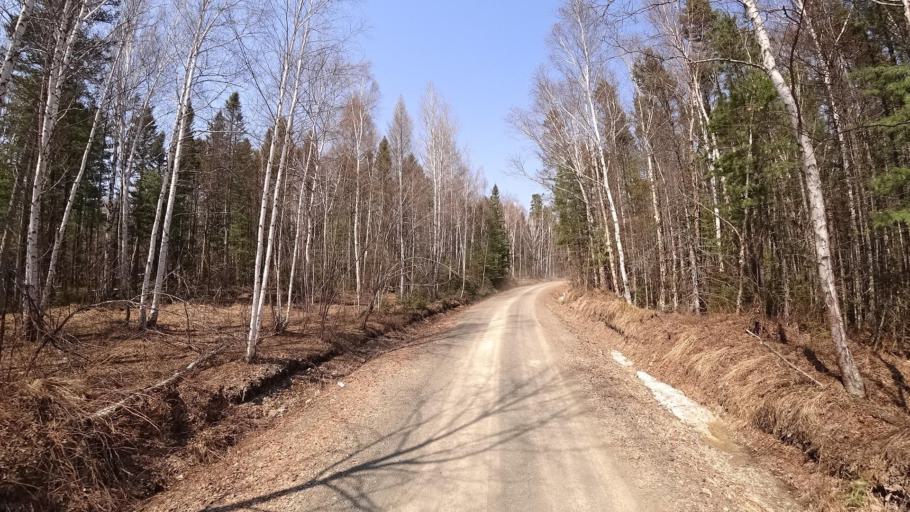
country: RU
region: Khabarovsk Krai
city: Selikhino
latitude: 50.6304
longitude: 137.4055
